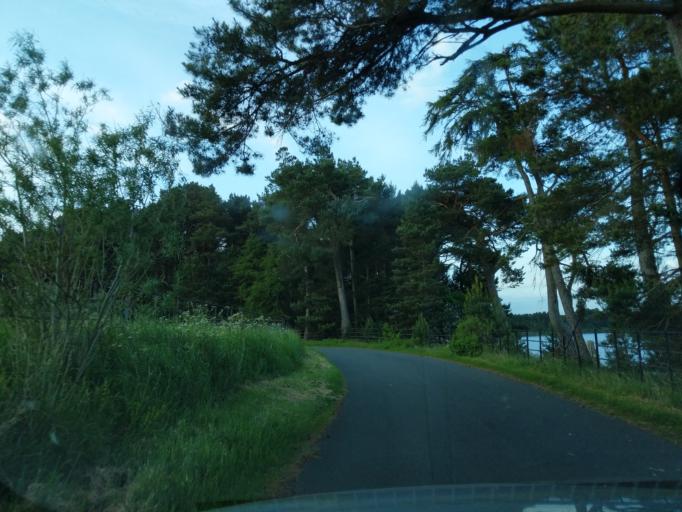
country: GB
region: Scotland
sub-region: Midlothian
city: Bonnyrigg
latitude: 55.7761
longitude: -3.1184
